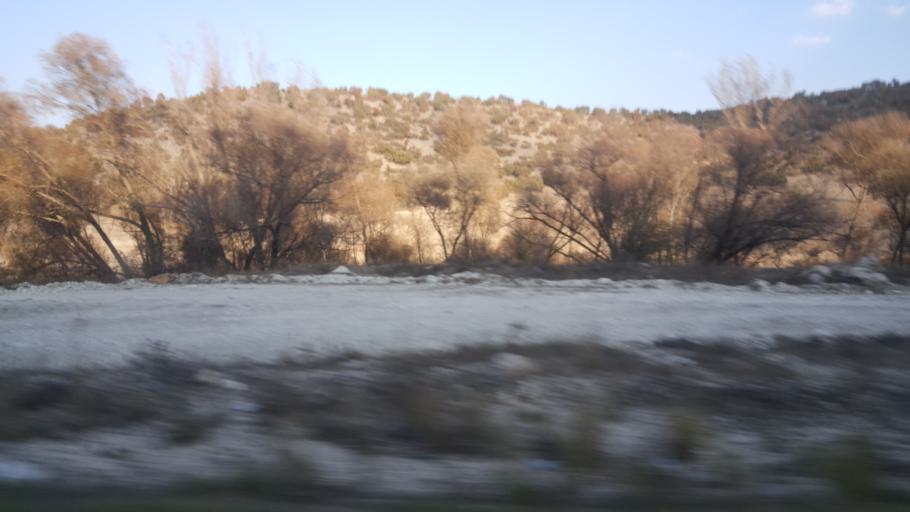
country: TR
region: Eskisehir
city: Kirka
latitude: 39.3522
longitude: 30.5865
